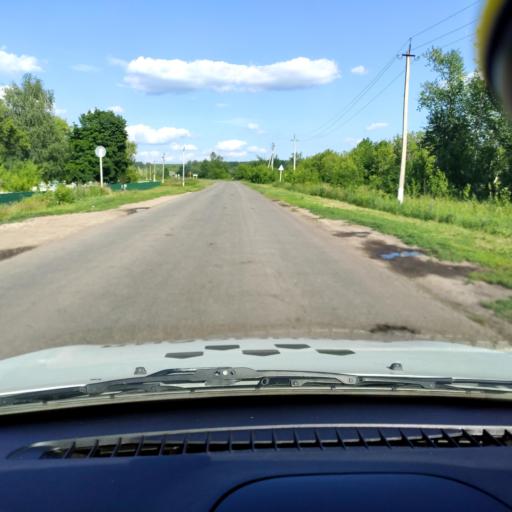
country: RU
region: Samara
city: Zhigulevsk
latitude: 53.3541
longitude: 49.3238
